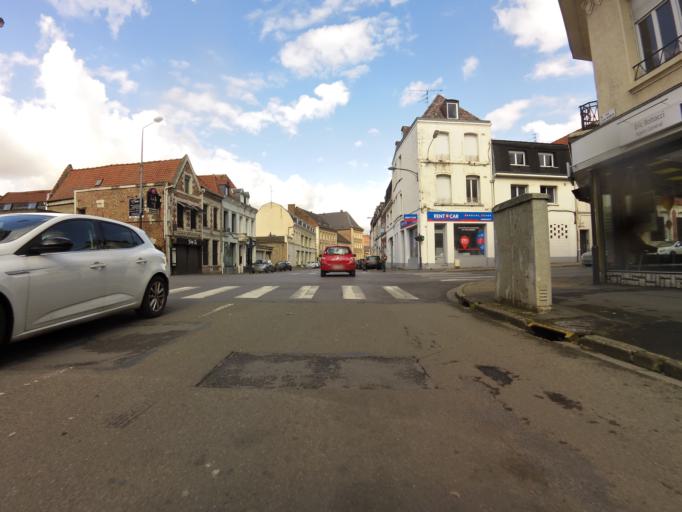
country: FR
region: Nord-Pas-de-Calais
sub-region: Departement du Nord
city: Neuville-Saint-Remy
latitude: 50.1764
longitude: 3.2275
